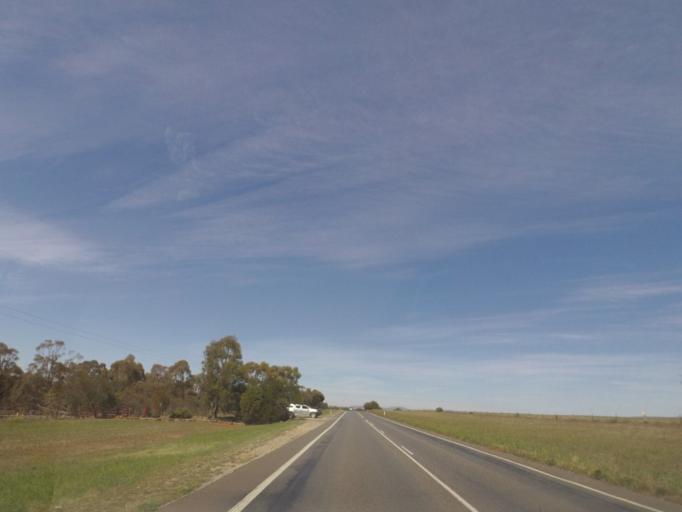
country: AU
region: Victoria
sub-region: Moorabool
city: Bacchus Marsh
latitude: -37.7866
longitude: 144.4243
